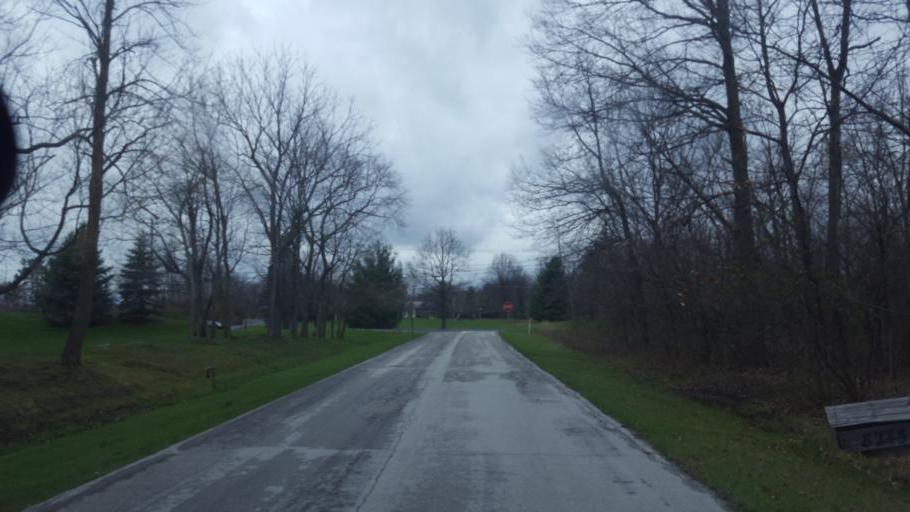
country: US
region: Ohio
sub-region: Delaware County
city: Sunbury
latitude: 40.1908
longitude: -82.8946
